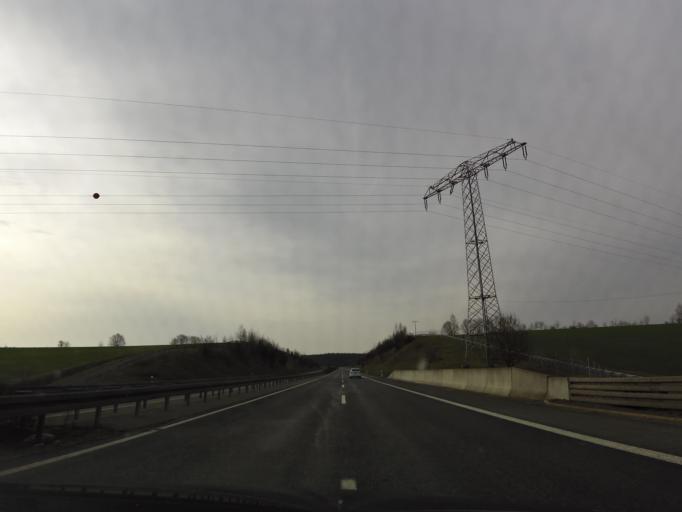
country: DE
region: Thuringia
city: Eisfeld
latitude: 50.4287
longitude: 10.8870
